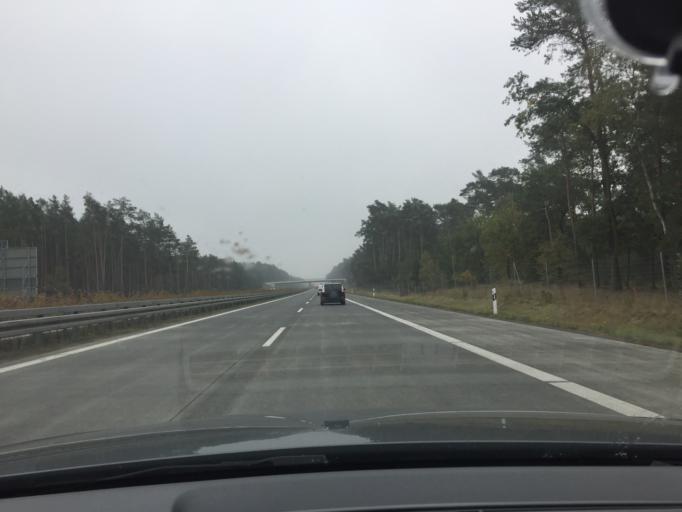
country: DE
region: Brandenburg
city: Luebben
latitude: 51.8850
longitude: 13.8567
